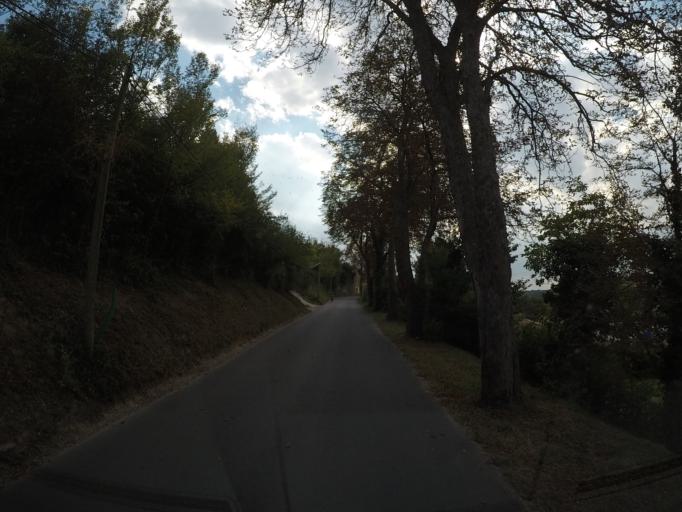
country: FR
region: Provence-Alpes-Cote d'Azur
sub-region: Departement des Alpes-de-Haute-Provence
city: Valensole
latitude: 43.8373
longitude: 5.9908
